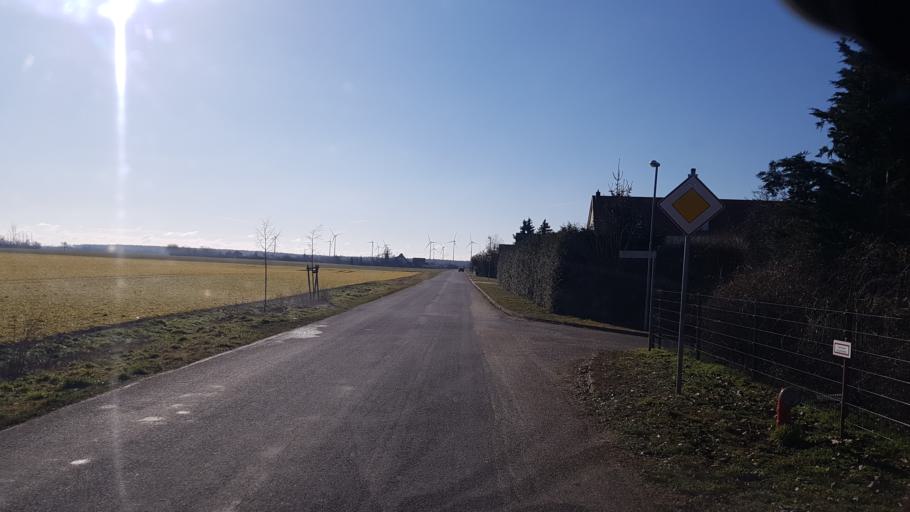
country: DE
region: Brandenburg
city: Muhlberg
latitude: 51.5028
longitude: 13.2318
